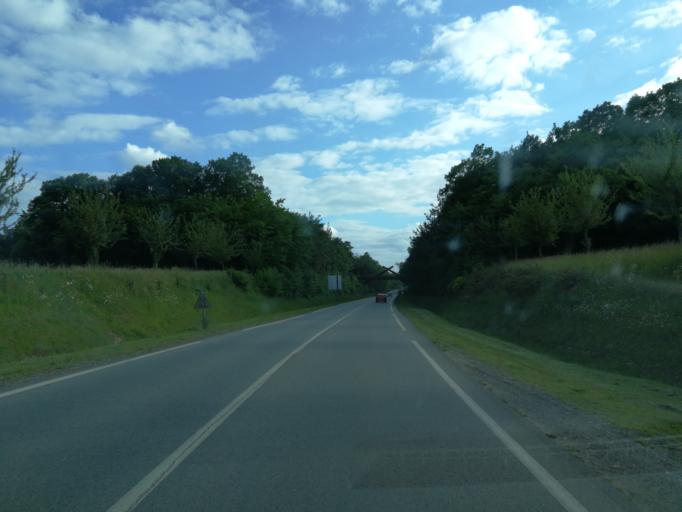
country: FR
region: Haute-Normandie
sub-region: Departement de l'Eure
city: Conches-en-Ouche
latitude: 48.9719
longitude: 0.9388
